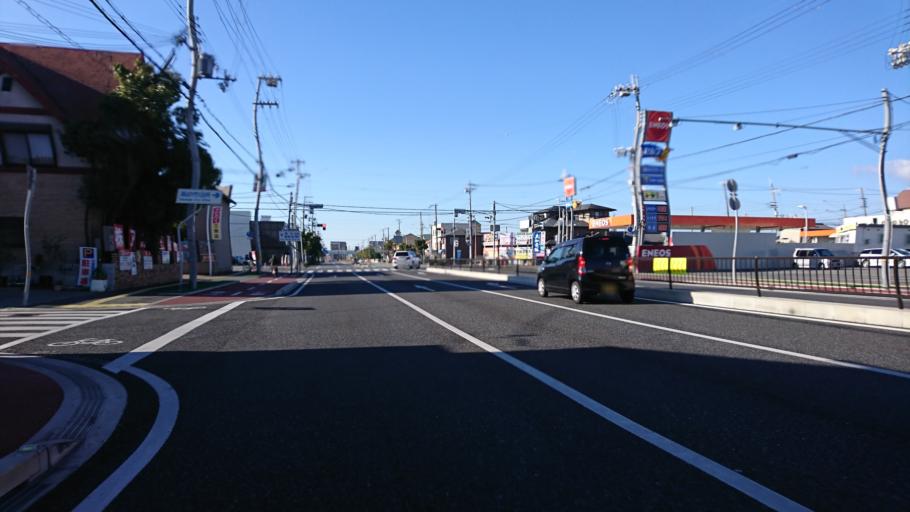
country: JP
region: Hyogo
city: Kakogawacho-honmachi
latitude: 34.7625
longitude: 134.8001
